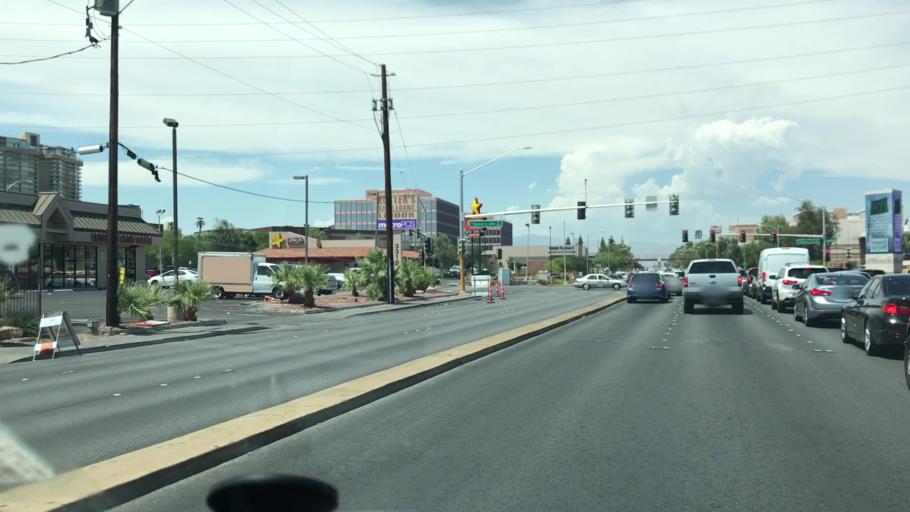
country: US
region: Nevada
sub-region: Clark County
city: Winchester
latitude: 36.1290
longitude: -115.1370
